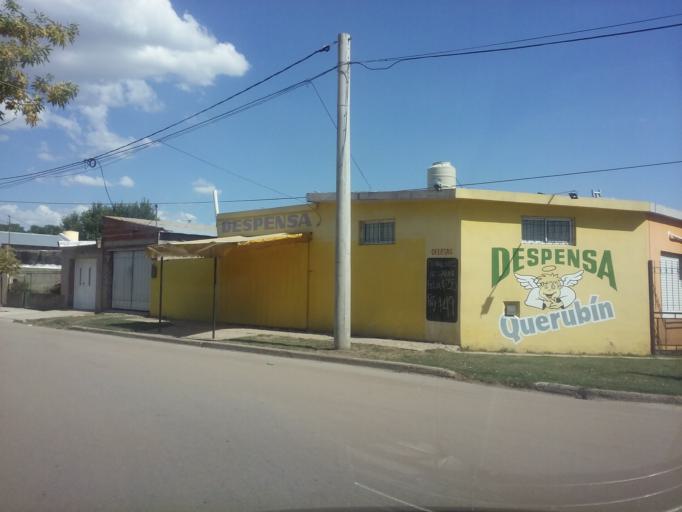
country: AR
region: La Pampa
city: Santa Rosa
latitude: -36.6434
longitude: -64.2986
